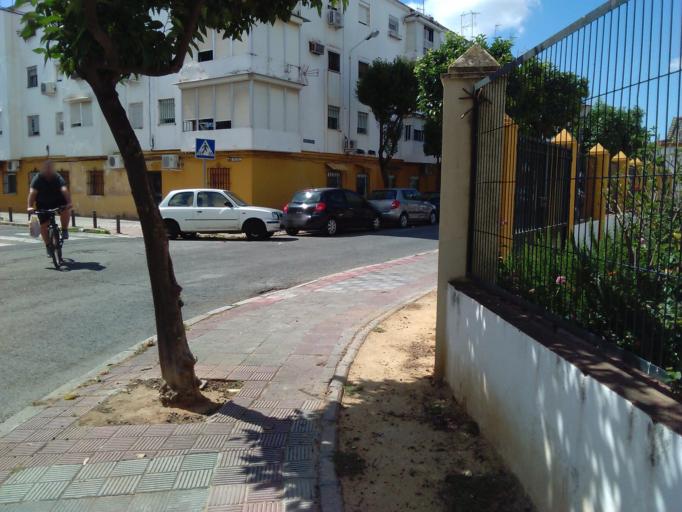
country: ES
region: Andalusia
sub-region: Provincia de Sevilla
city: La Algaba
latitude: 37.4278
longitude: -5.9831
